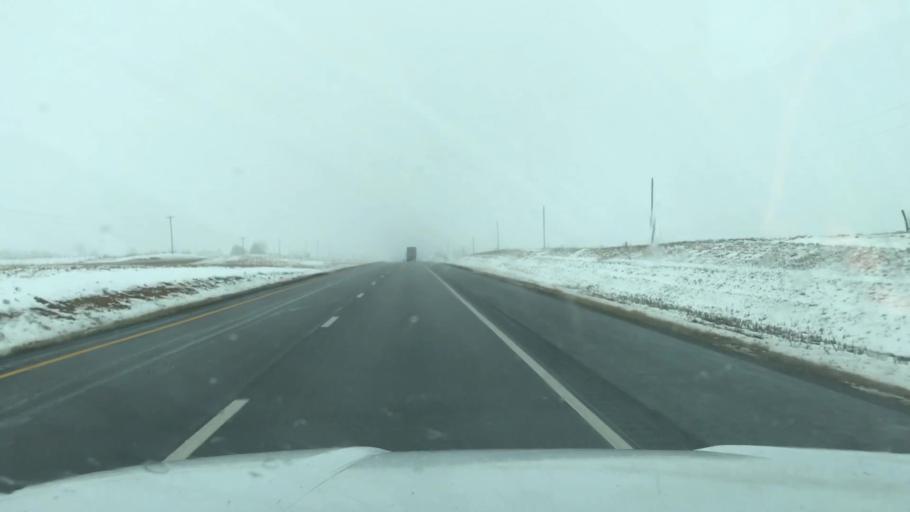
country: US
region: Missouri
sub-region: Clinton County
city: Gower
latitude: 39.7619
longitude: -94.5238
